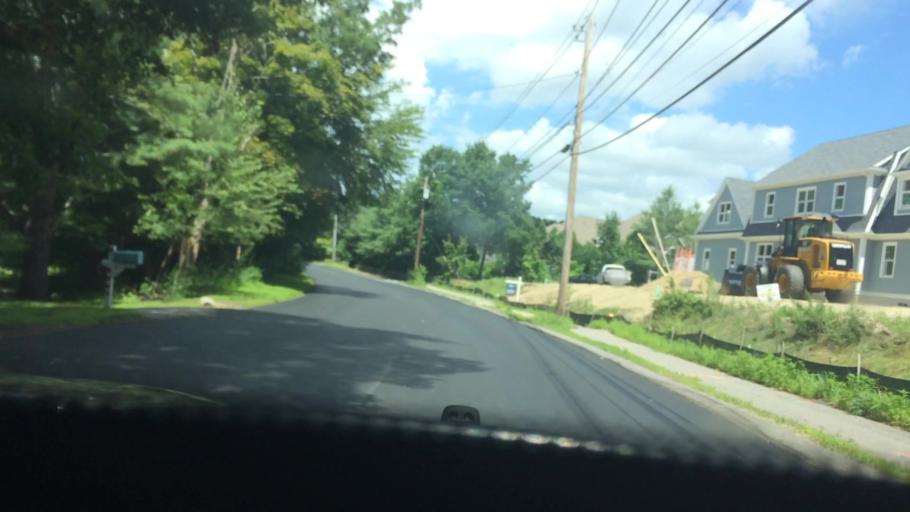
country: US
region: Massachusetts
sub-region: Middlesex County
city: Sudbury
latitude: 42.4039
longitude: -71.4365
